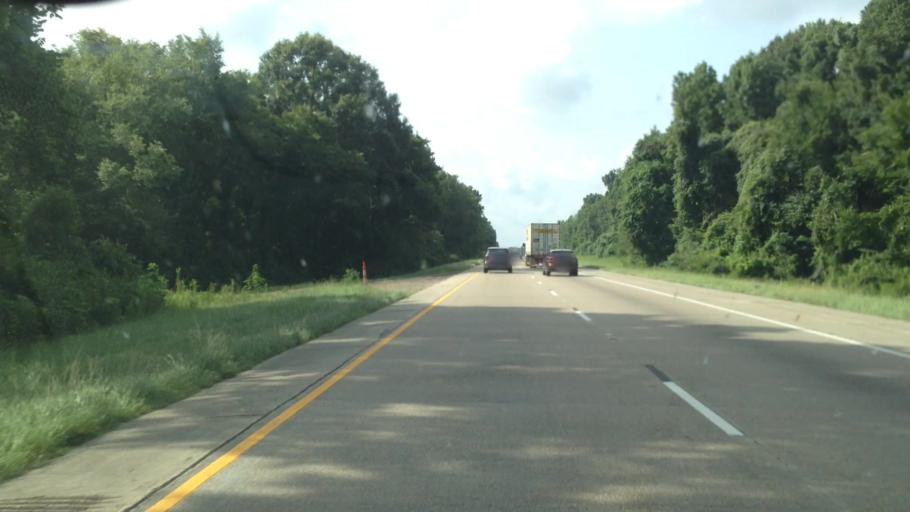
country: US
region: Louisiana
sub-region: Ascension Parish
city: Prairieville
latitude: 30.3001
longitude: -90.9928
